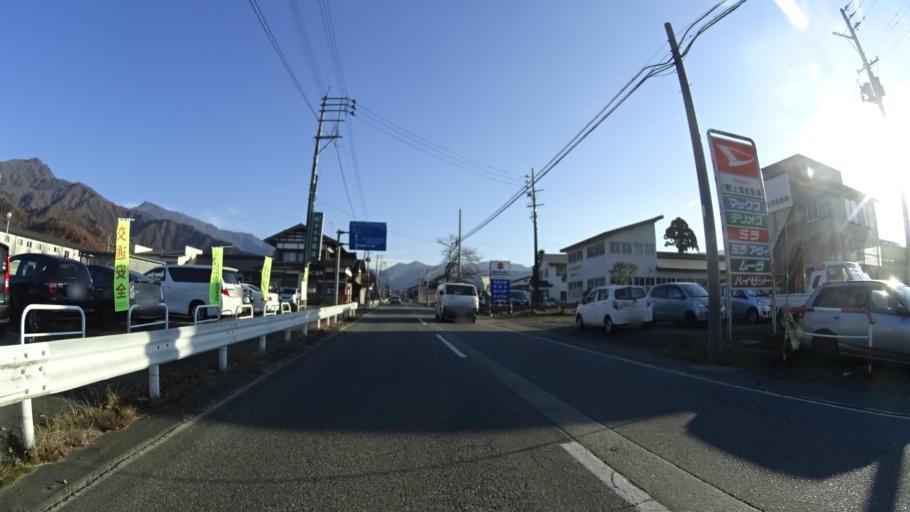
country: JP
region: Niigata
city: Shiozawa
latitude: 37.0225
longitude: 138.8651
